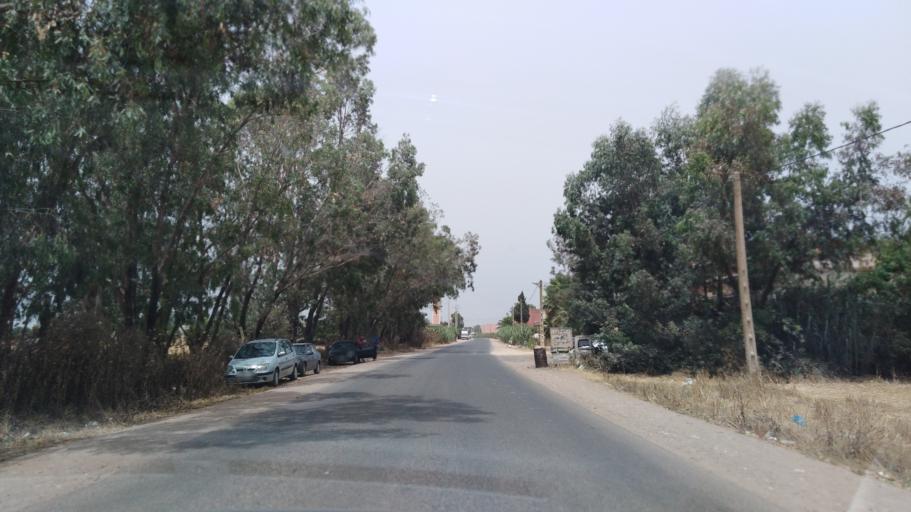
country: MA
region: Grand Casablanca
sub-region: Mediouna
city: Mediouna
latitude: 33.3979
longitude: -7.5111
